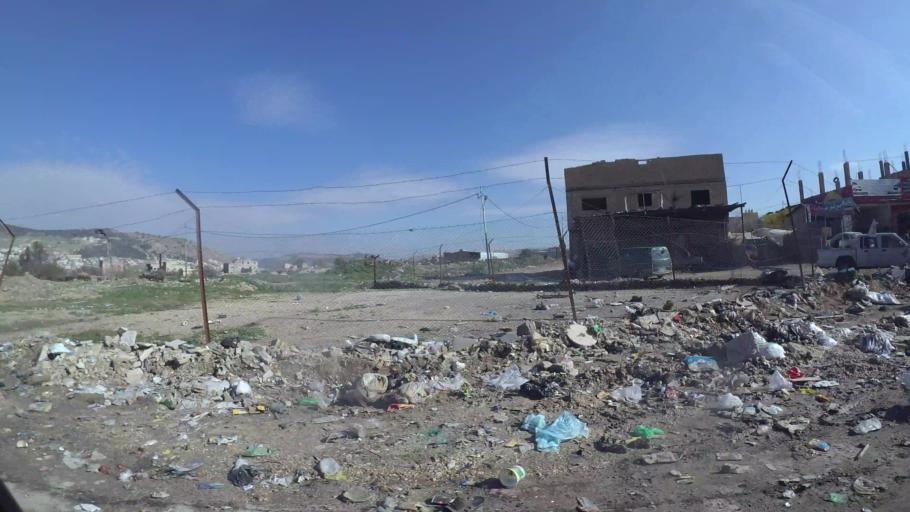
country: JO
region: Amman
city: Al Jubayhah
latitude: 32.0802
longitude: 35.8472
